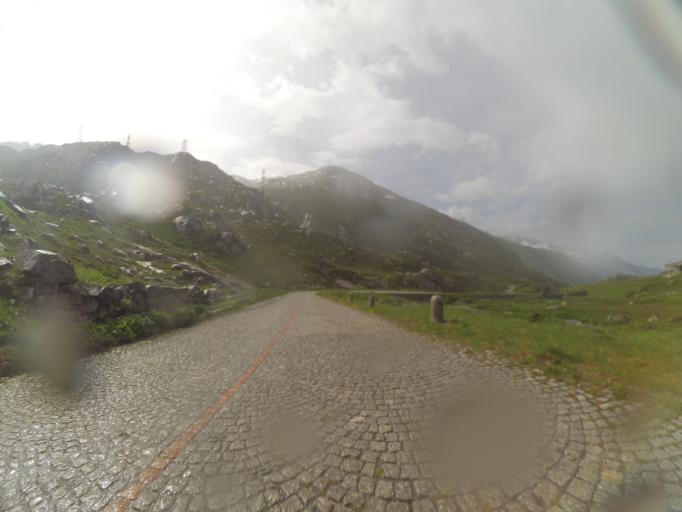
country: CH
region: Ticino
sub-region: Leventina District
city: Airolo
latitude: 46.5748
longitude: 8.5592
